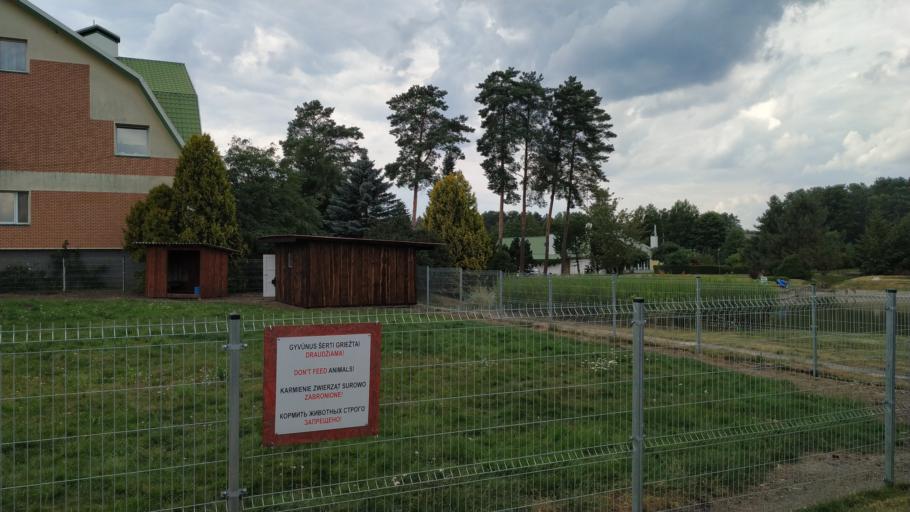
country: LT
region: Alytaus apskritis
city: Druskininkai
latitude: 54.0232
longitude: 24.0795
